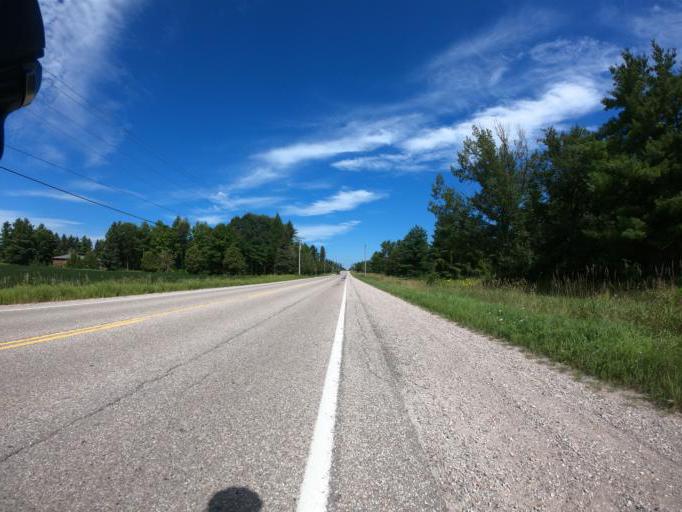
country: CA
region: Ontario
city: Waterloo
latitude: 43.5153
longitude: -80.3947
